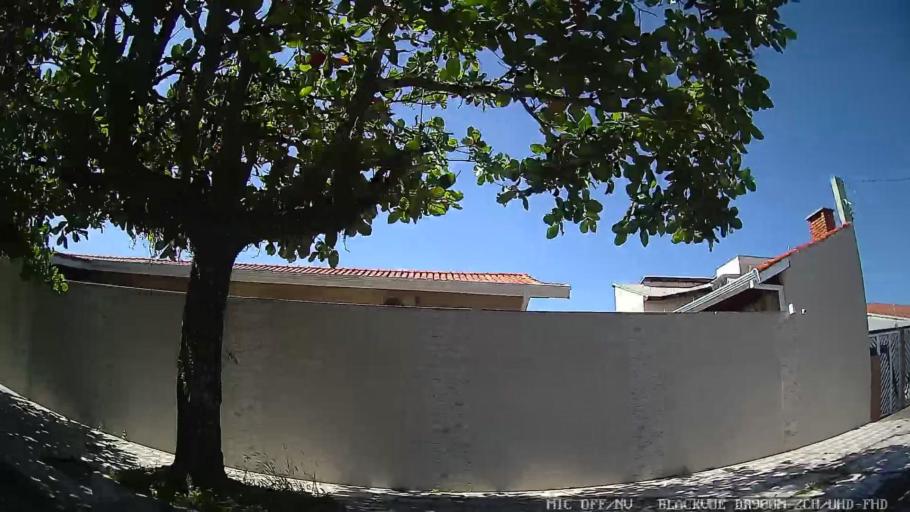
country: BR
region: Sao Paulo
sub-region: Peruibe
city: Peruibe
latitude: -24.3170
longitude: -46.9901
